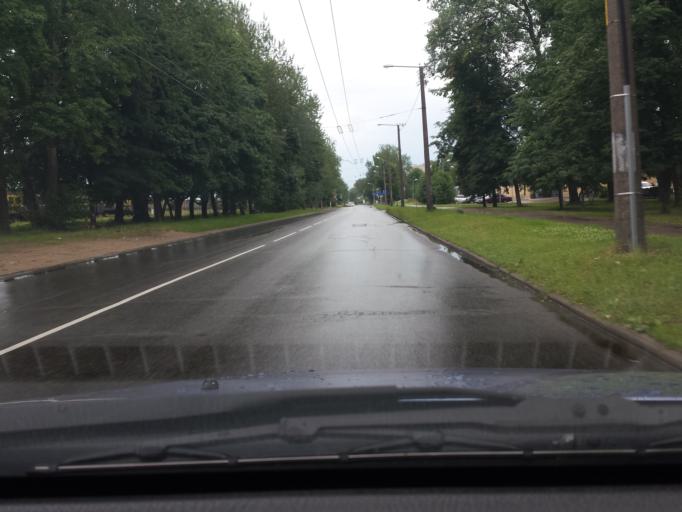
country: LV
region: Kekava
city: Balozi
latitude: 56.9187
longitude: 24.1854
